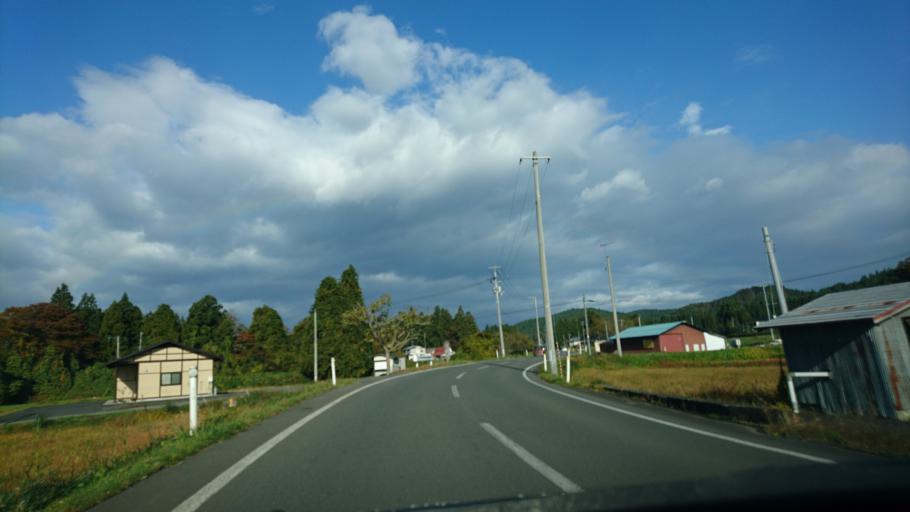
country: JP
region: Iwate
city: Mizusawa
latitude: 39.0502
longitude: 141.0470
